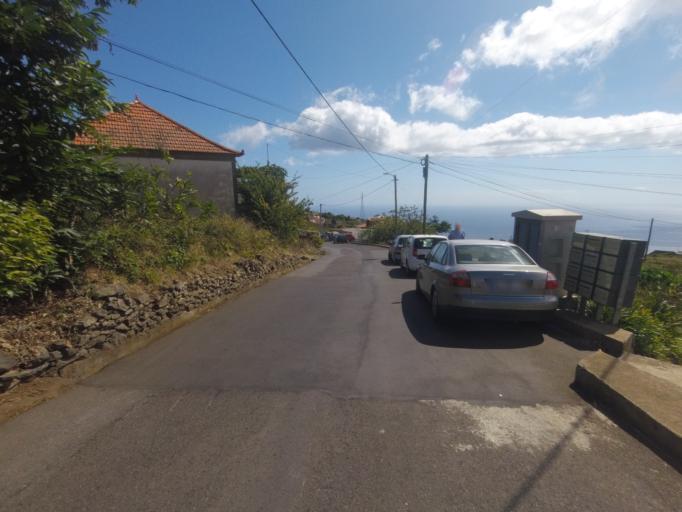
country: PT
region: Madeira
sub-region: Ribeira Brava
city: Campanario
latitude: 32.6804
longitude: -17.0441
